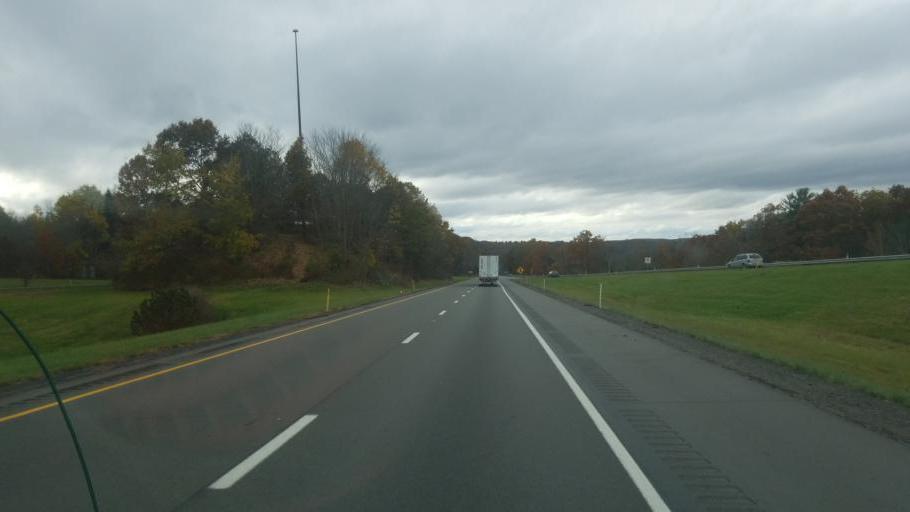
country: US
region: Pennsylvania
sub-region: Clarion County
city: Clarion
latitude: 41.1861
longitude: -79.3957
